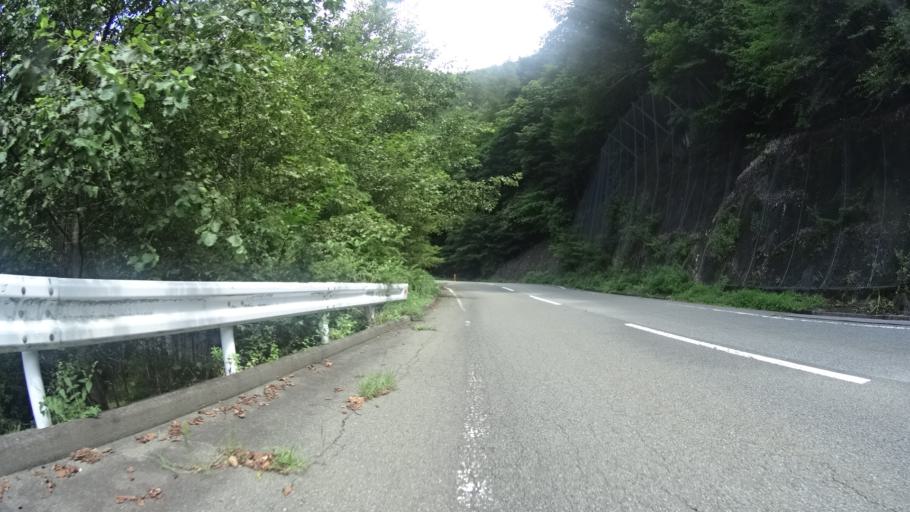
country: JP
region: Yamanashi
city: Enzan
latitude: 35.7997
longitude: 138.6740
